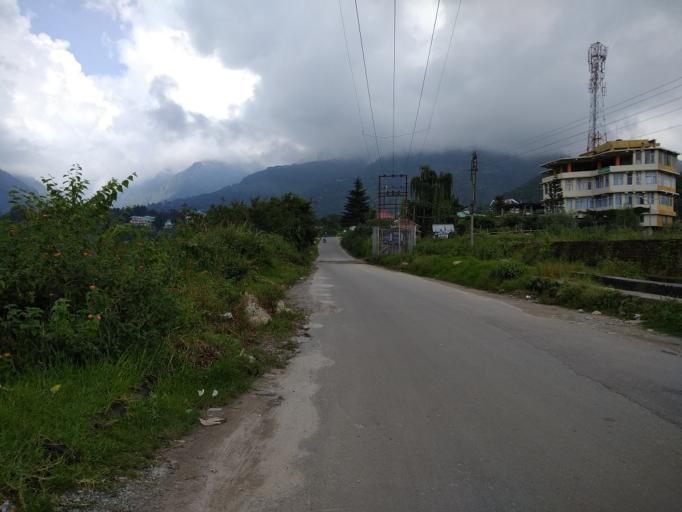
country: IN
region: Himachal Pradesh
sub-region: Kangra
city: Palampur
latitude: 32.1275
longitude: 76.5341
